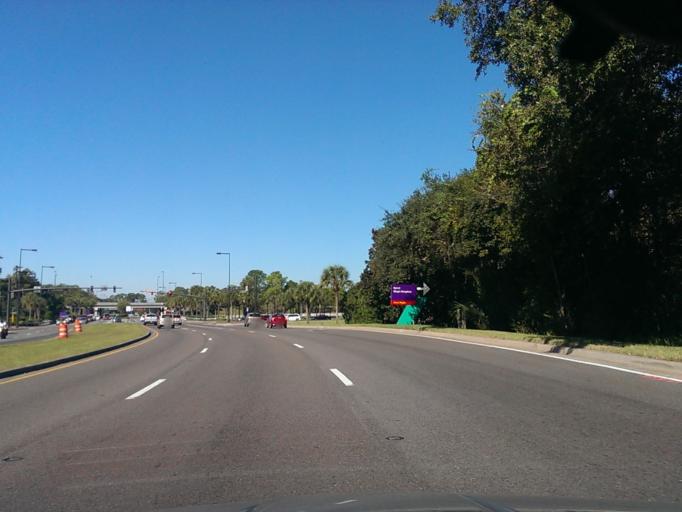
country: US
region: Florida
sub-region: Osceola County
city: Celebration
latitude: 28.3696
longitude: -81.5336
